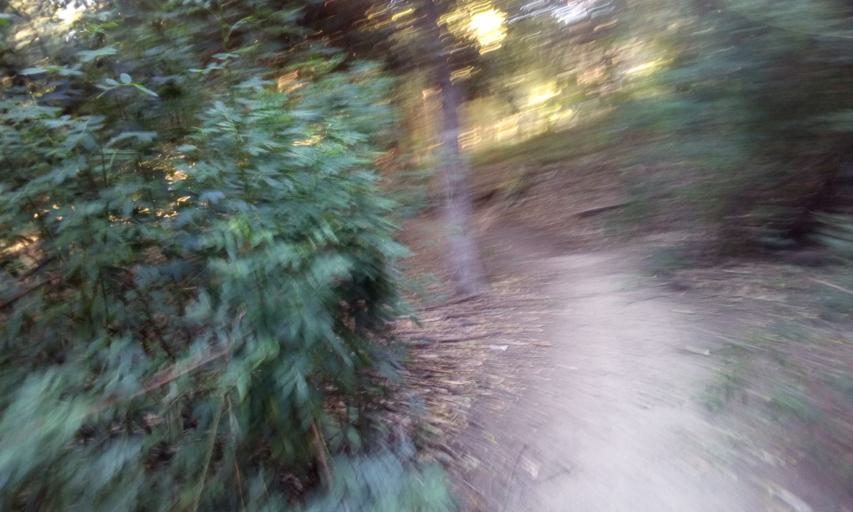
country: AU
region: New South Wales
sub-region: Wollongong
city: Keiraville
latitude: -34.4096
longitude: 150.8616
